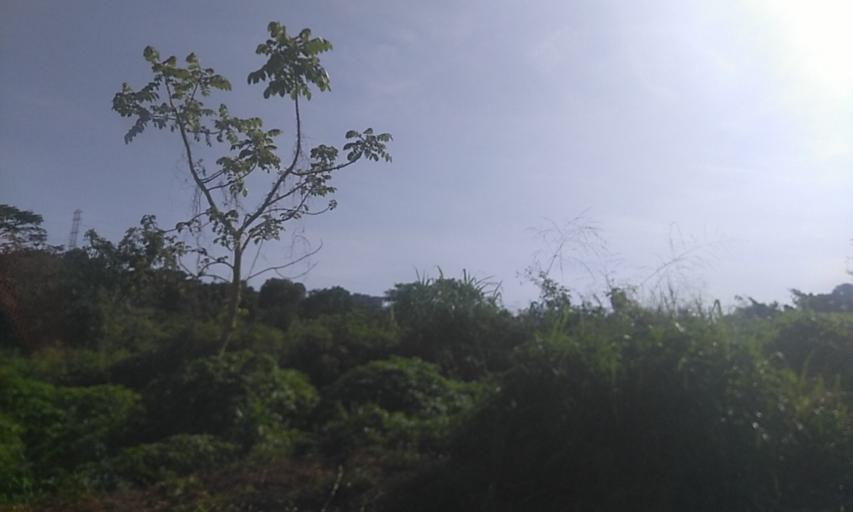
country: UG
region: Central Region
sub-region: Wakiso District
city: Kireka
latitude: 0.3636
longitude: 32.6313
